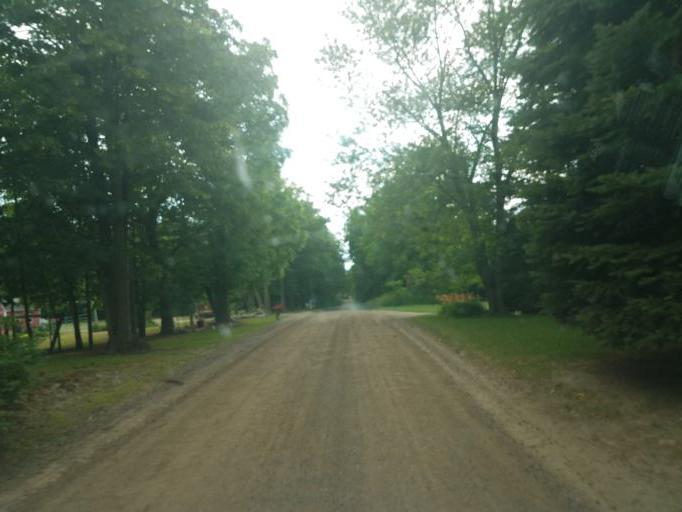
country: US
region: Michigan
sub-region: Barry County
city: Nashville
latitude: 42.5970
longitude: -84.9808
